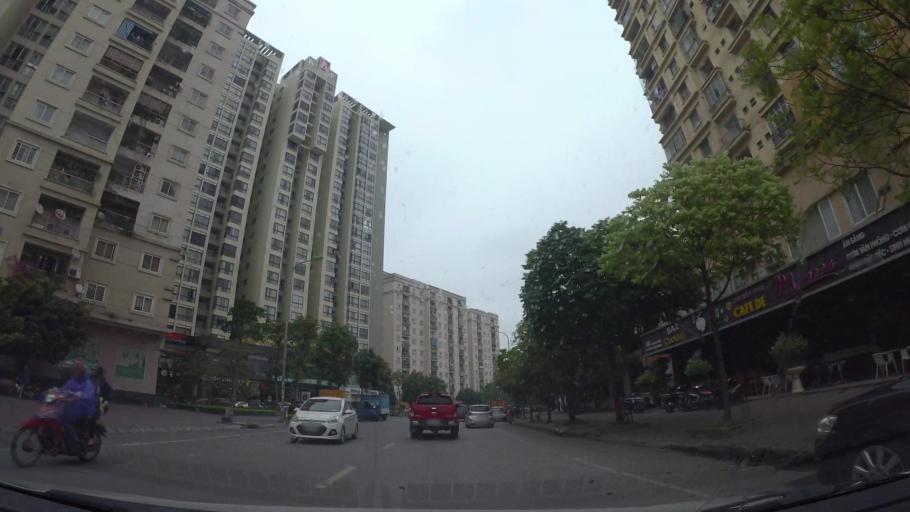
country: VN
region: Ha Noi
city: Cau Giay
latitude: 21.0178
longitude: 105.7987
